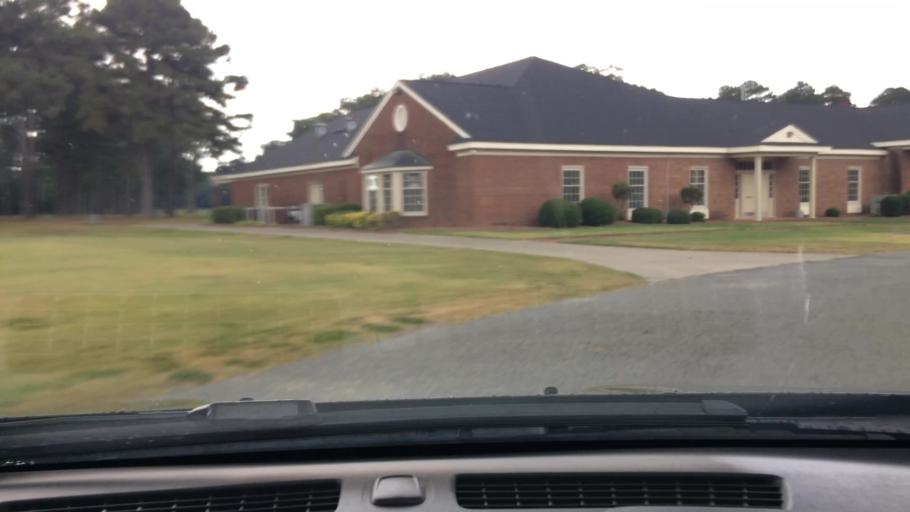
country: US
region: North Carolina
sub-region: Pitt County
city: Ayden
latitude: 35.4634
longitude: -77.3899
